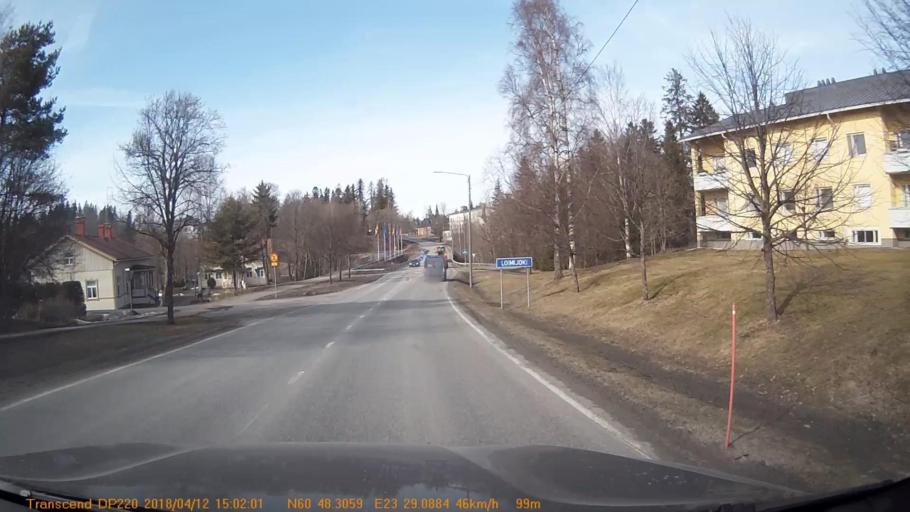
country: FI
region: Haeme
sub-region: Forssa
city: Jokioinen
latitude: 60.8051
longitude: 23.4849
